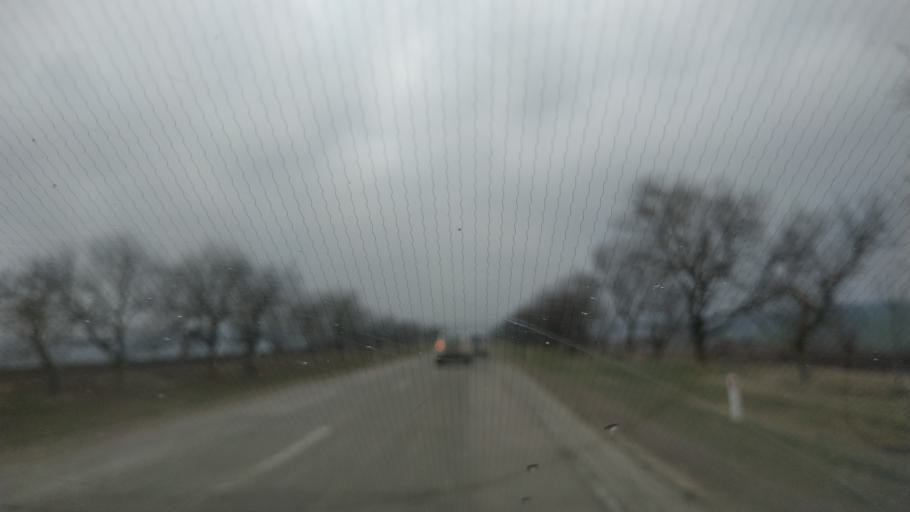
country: MD
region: Gagauzia
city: Comrat
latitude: 46.2545
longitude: 28.7549
